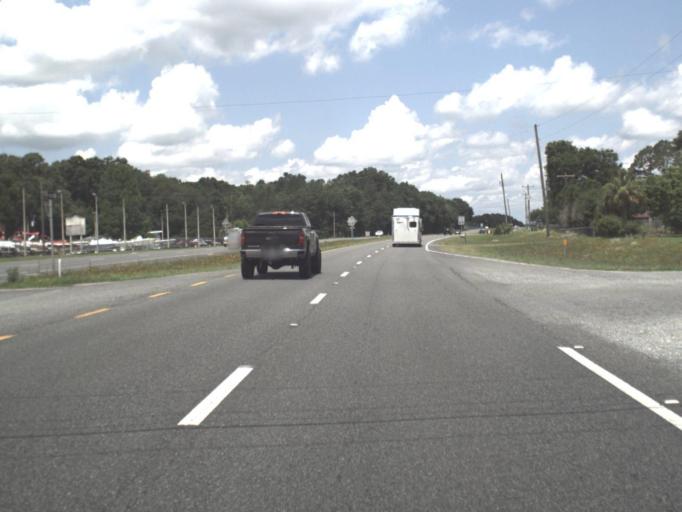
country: US
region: Florida
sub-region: Alachua County
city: High Springs
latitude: 29.8112
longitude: -82.5598
